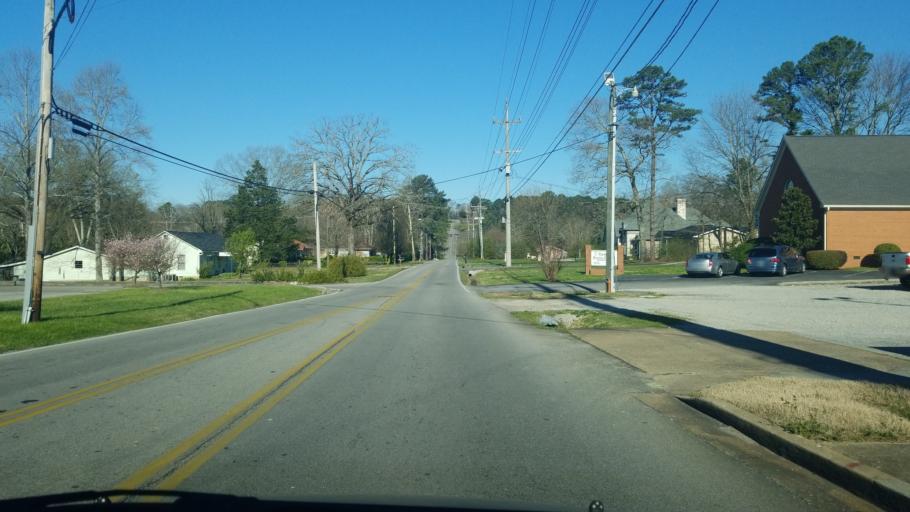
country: US
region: Tennessee
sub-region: Hamilton County
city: East Brainerd
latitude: 35.0271
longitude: -85.1579
